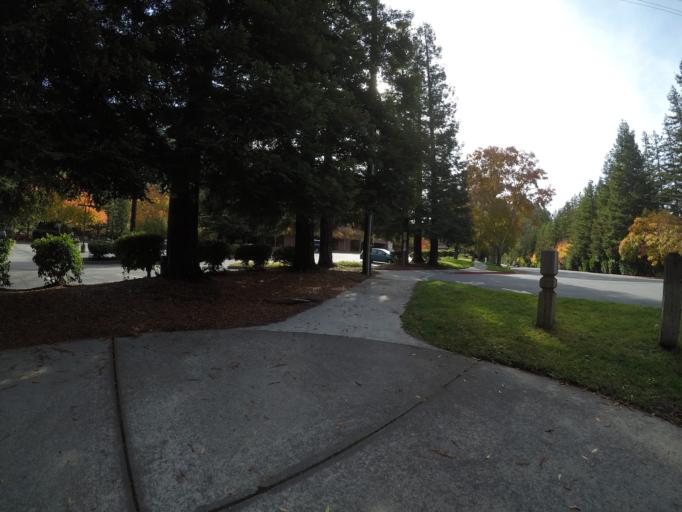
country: US
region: California
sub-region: Santa Cruz County
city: Scotts Valley
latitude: 37.0531
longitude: -122.0082
